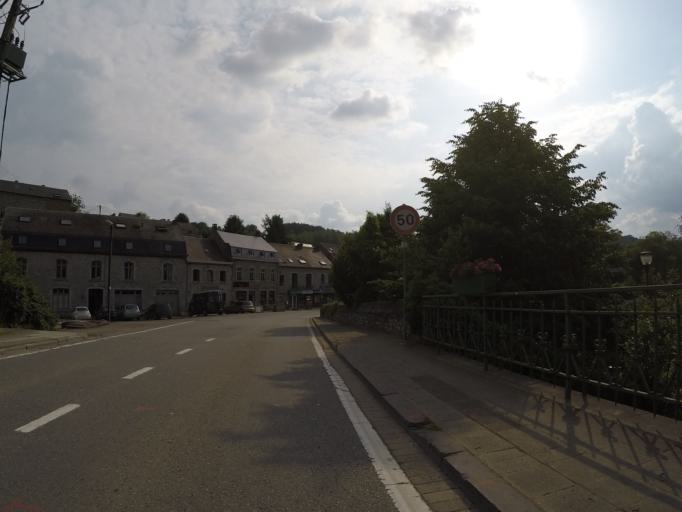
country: BE
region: Wallonia
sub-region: Province de Namur
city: Assesse
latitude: 50.3225
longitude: 5.0086
